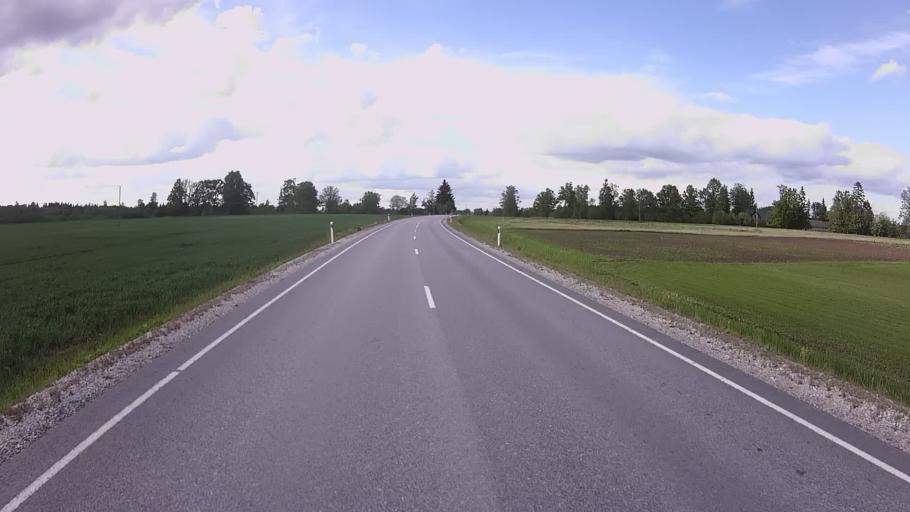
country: EE
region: Jogevamaa
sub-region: Mustvee linn
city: Mustvee
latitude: 58.8877
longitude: 26.8125
